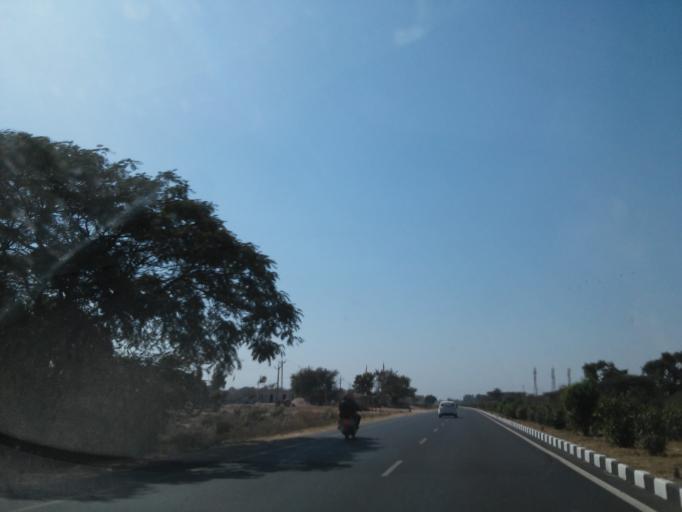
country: IN
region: Gujarat
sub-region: Sabar Kantha
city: Himatnagar
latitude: 23.5115
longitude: 72.9279
